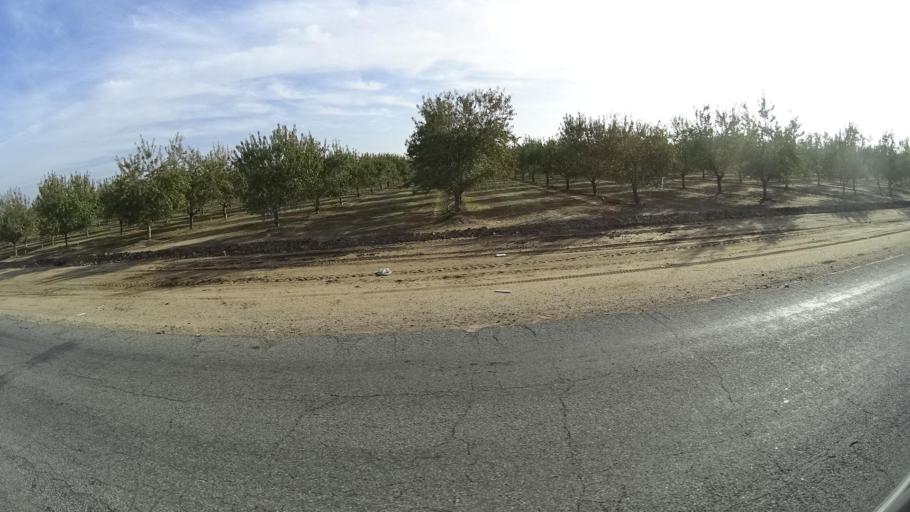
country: US
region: California
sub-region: Kern County
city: McFarland
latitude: 35.6844
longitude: -119.2048
